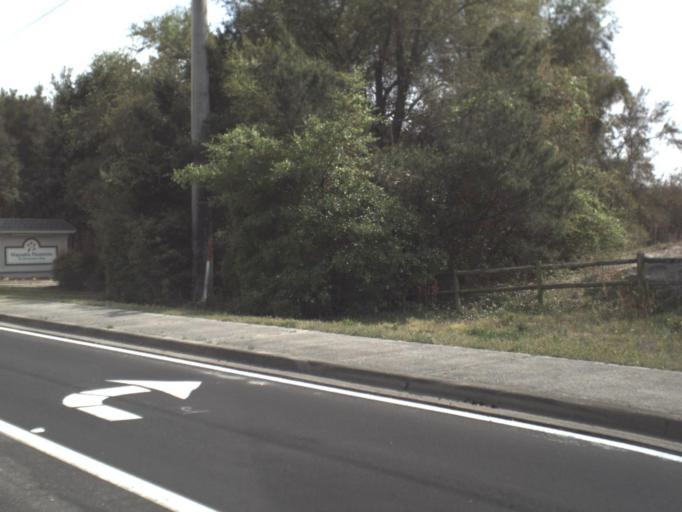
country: US
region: Florida
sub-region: Okaloosa County
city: Niceville
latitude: 30.4934
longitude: -86.4302
